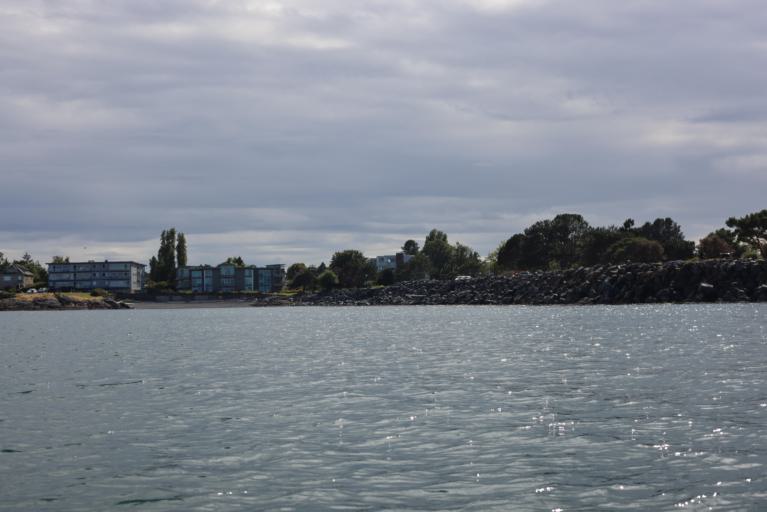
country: CA
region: British Columbia
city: Oak Bay
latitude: 48.4253
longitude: -123.2983
